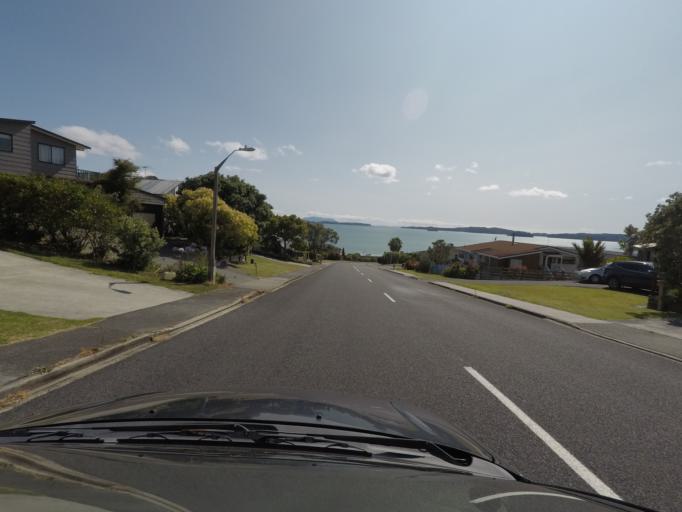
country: NZ
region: Auckland
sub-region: Auckland
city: Warkworth
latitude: -36.4317
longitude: 174.7390
